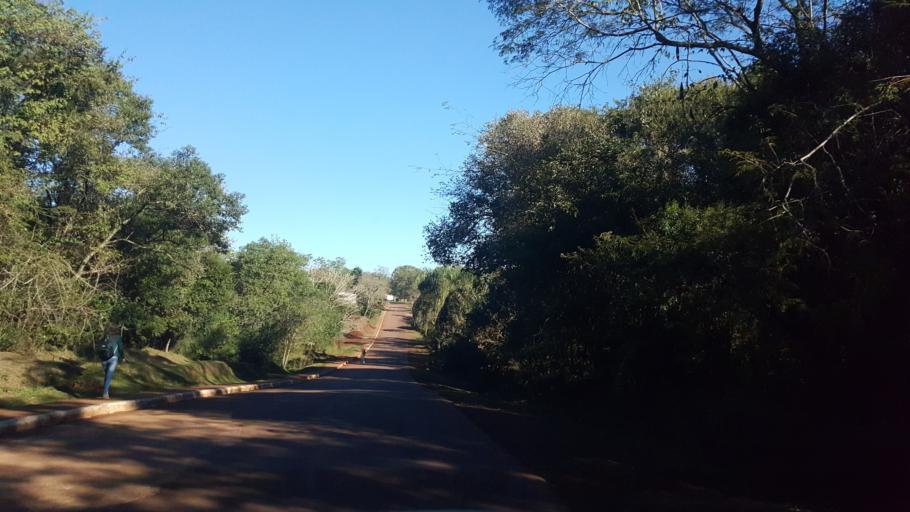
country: AR
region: Misiones
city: Jardin America
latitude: -27.0890
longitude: -55.2864
